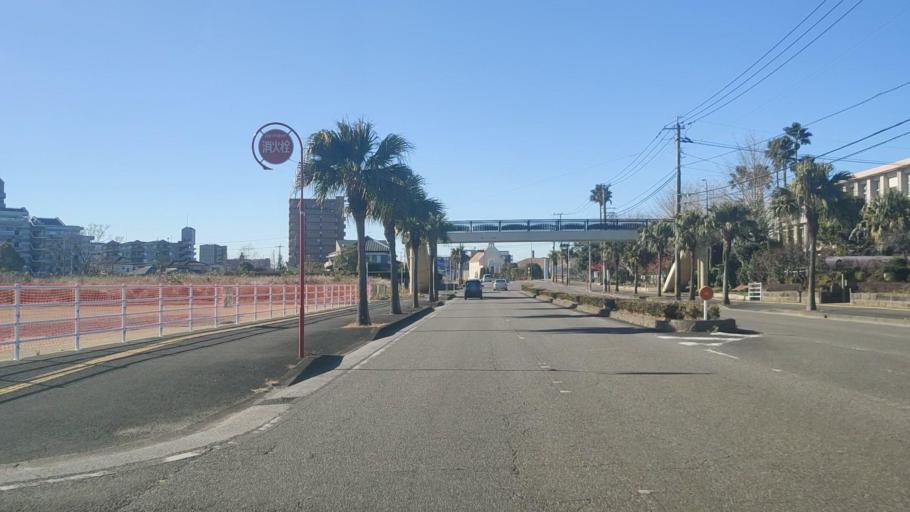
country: JP
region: Miyazaki
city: Miyazaki-shi
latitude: 31.9428
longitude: 131.4362
